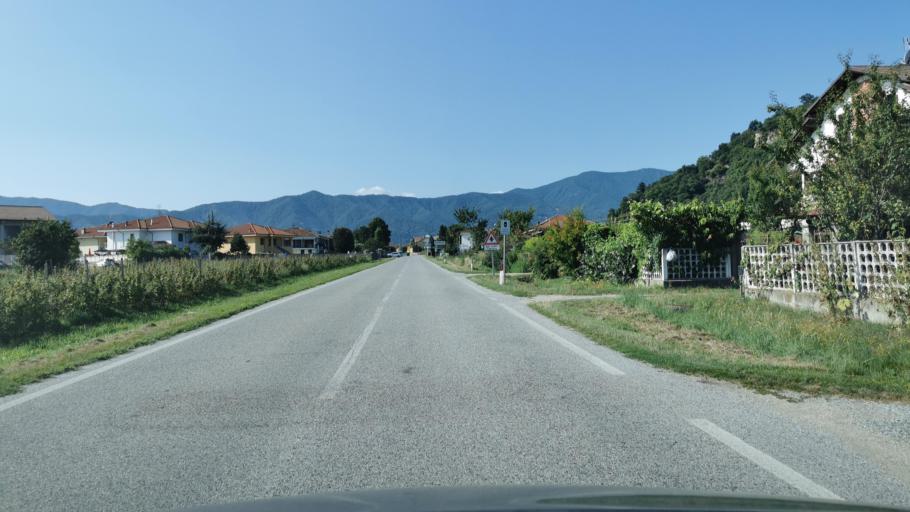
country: IT
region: Piedmont
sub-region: Provincia di Cuneo
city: Revello
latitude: 44.6621
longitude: 7.3944
